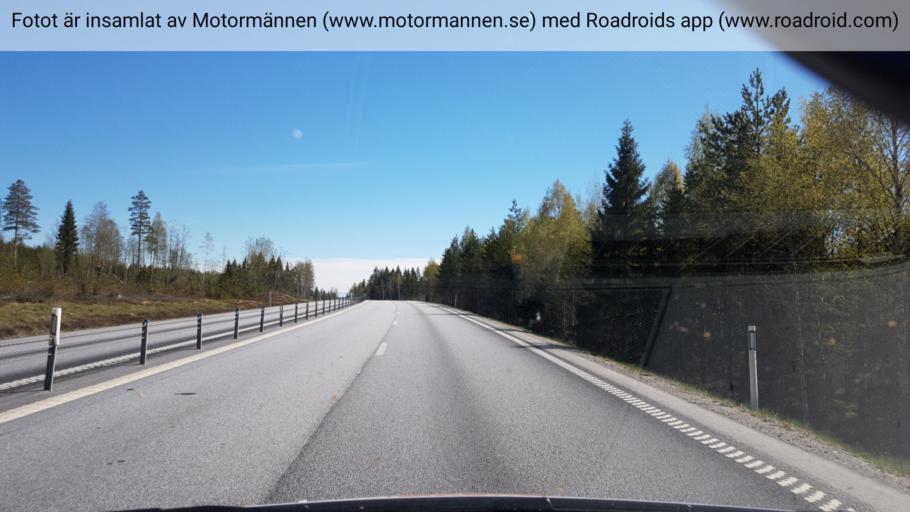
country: SE
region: Vaesterbotten
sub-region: Vannas Kommun
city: Vannasby
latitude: 63.9060
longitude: 19.8912
